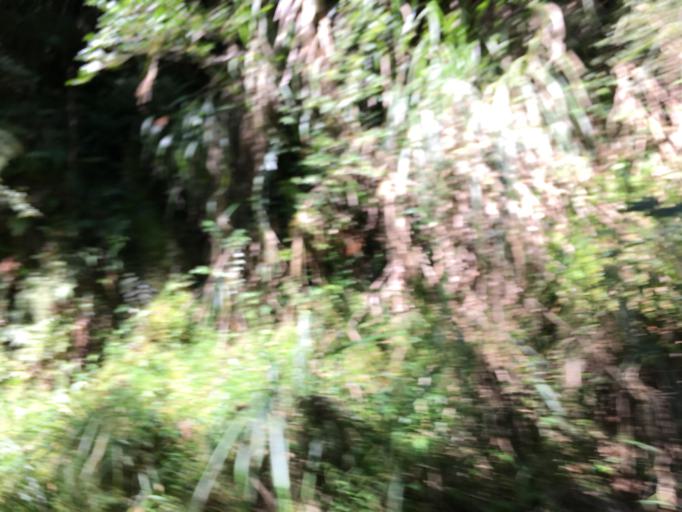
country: TW
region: Taiwan
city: Daxi
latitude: 24.5714
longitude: 121.4183
